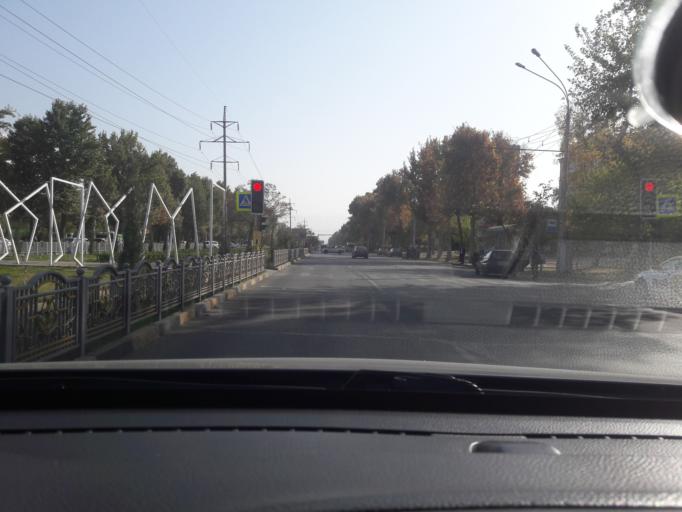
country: TJ
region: Dushanbe
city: Dushanbe
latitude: 38.5361
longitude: 68.7618
